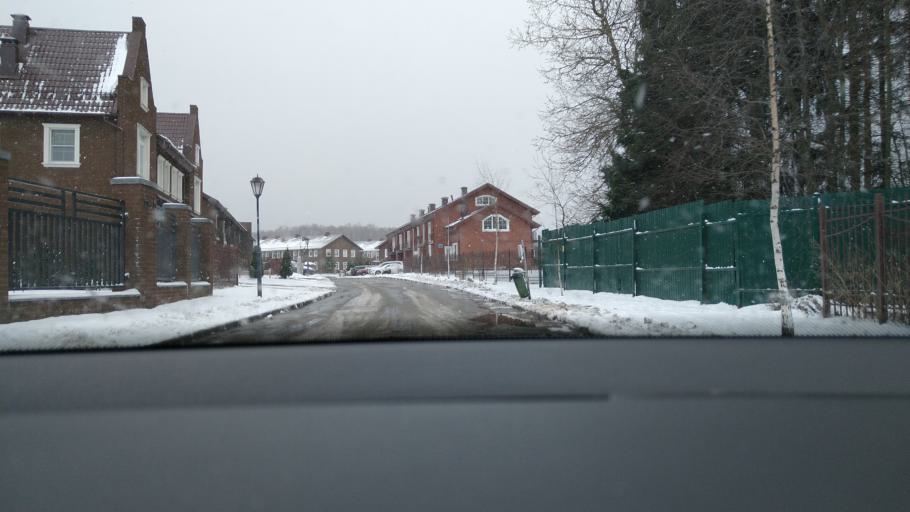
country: RU
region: Moskovskaya
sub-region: Leninskiy Rayon
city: Vnukovo
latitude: 55.6173
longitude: 37.3201
